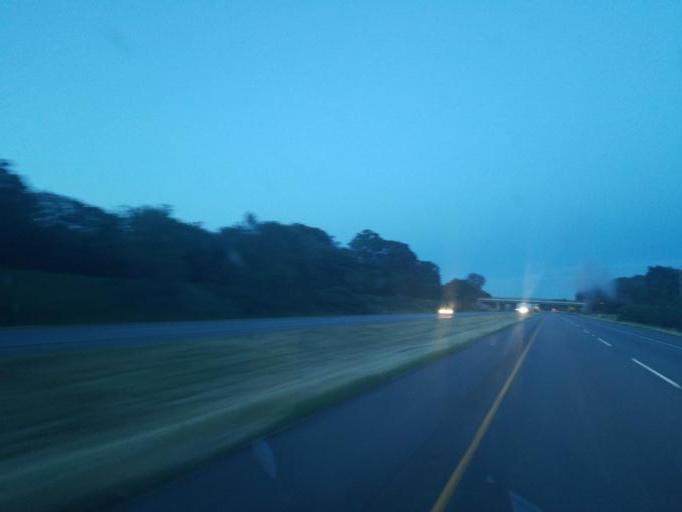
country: US
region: Indiana
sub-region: Saint Joseph County
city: Georgetown
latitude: 41.7161
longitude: -86.2211
